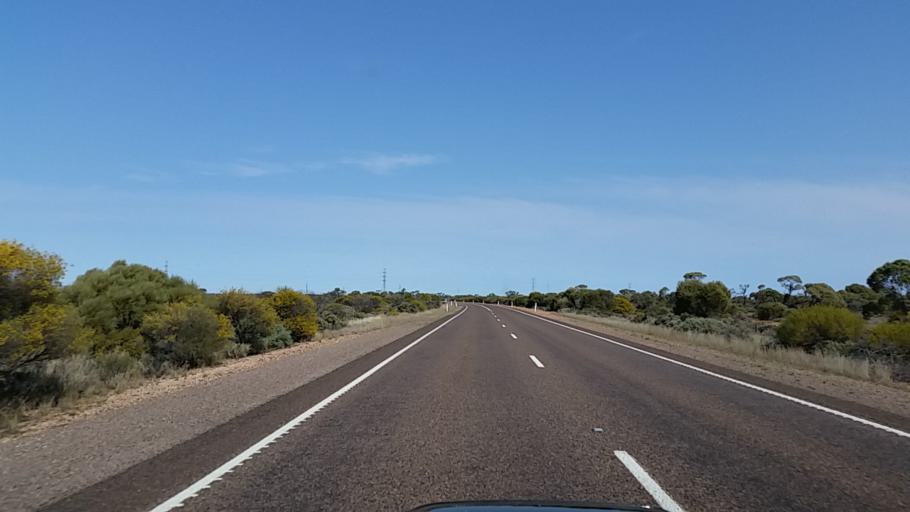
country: AU
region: South Australia
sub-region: Whyalla
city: Whyalla
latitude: -32.7224
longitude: 137.5083
